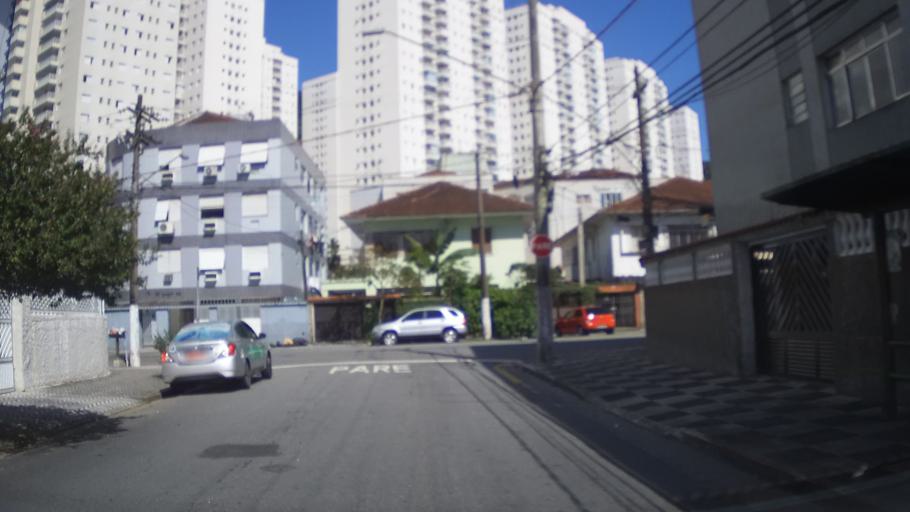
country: BR
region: Sao Paulo
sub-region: Santos
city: Santos
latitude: -23.9582
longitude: -46.3483
